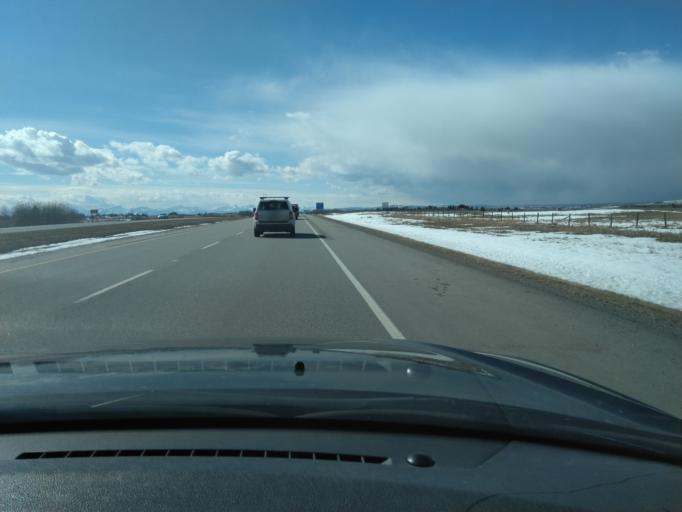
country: CA
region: Alberta
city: Cochrane
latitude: 51.1902
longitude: -114.3871
